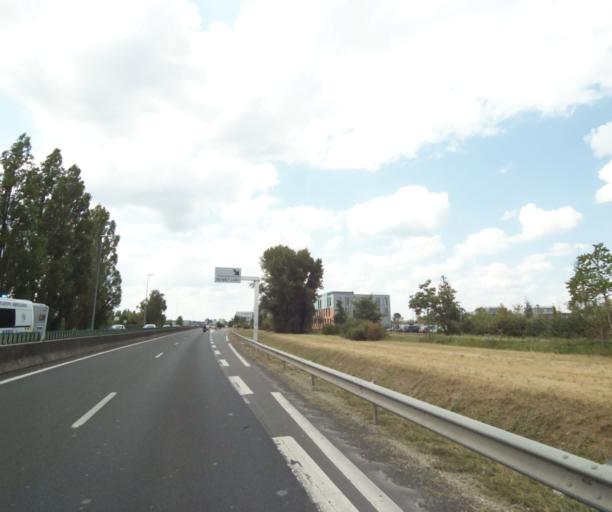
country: FR
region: Centre
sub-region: Departement du Loiret
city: Olivet
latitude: 47.8557
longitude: 1.9127
